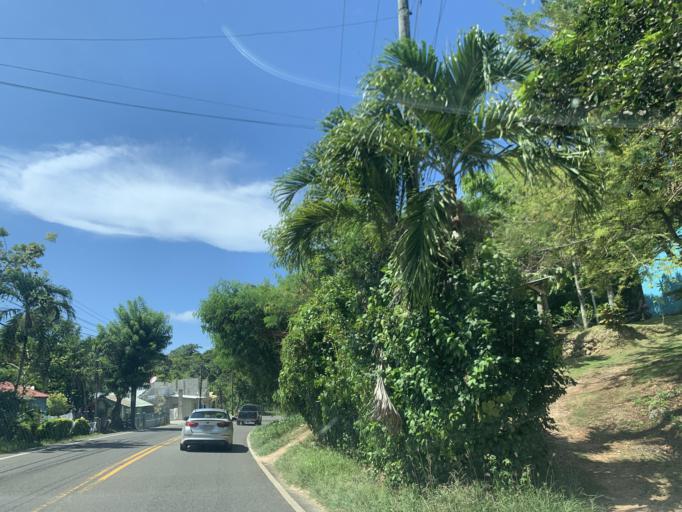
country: DO
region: Maria Trinidad Sanchez
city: Cabrera
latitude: 19.6521
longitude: -69.9332
